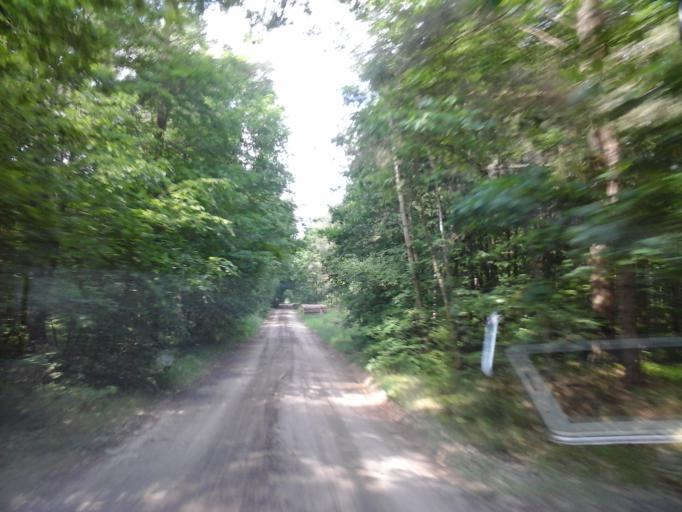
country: PL
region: Lubusz
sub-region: Powiat strzelecko-drezdenecki
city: Dobiegniew
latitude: 53.0605
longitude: 15.7693
